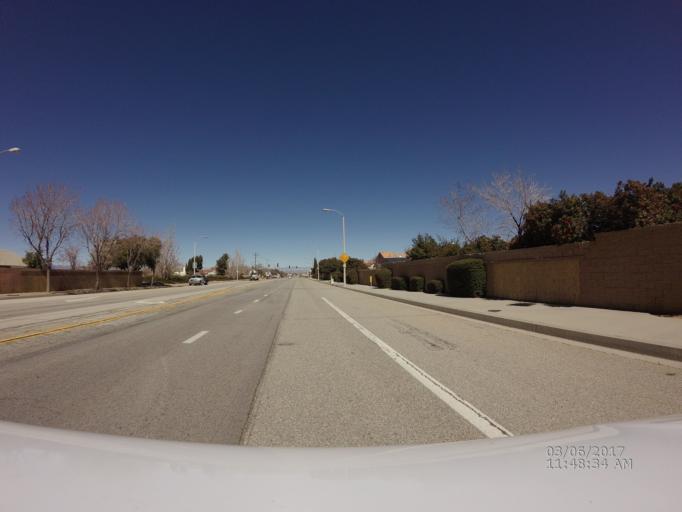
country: US
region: California
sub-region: Los Angeles County
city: Quartz Hill
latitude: 34.6514
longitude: -118.2361
